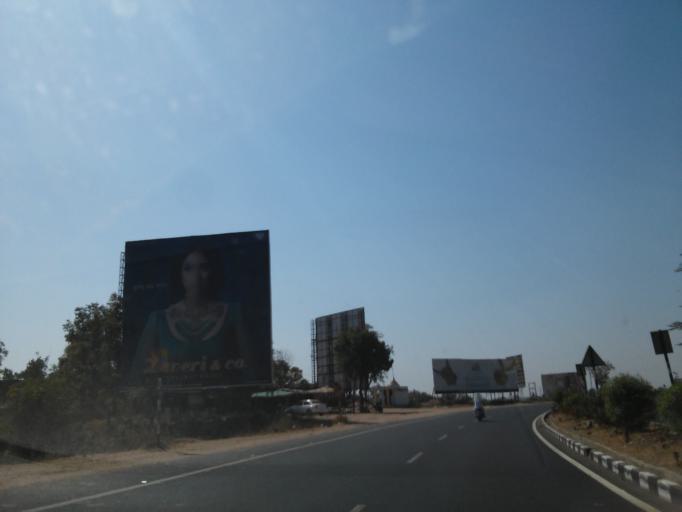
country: IN
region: Gujarat
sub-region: Mahesana
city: Vijapur
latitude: 23.4475
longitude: 72.8679
